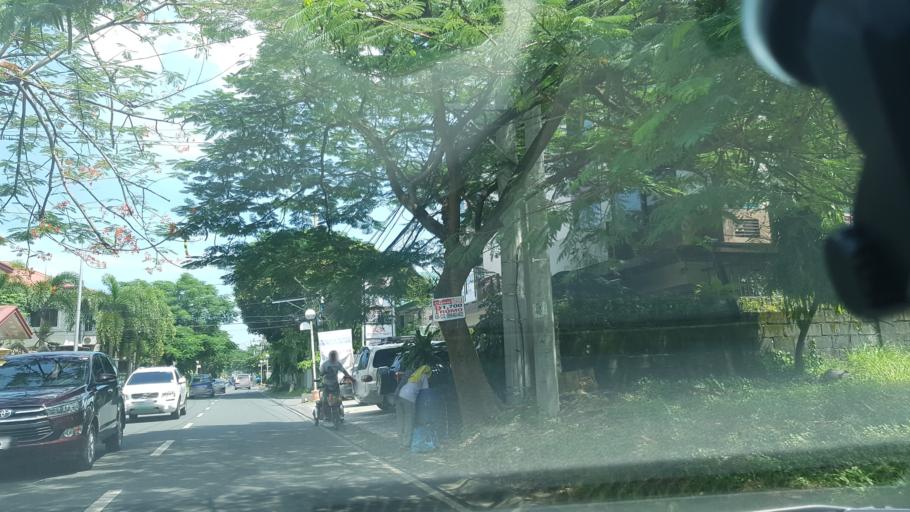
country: PH
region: Calabarzon
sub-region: Province of Rizal
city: Las Pinas
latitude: 14.4286
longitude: 120.9945
